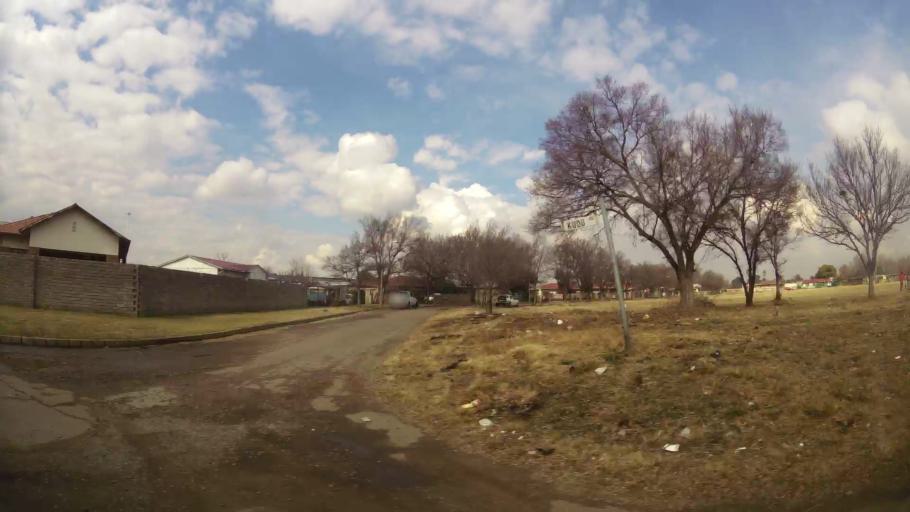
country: ZA
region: Gauteng
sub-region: Sedibeng District Municipality
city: Vereeniging
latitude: -26.6640
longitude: 27.9194
